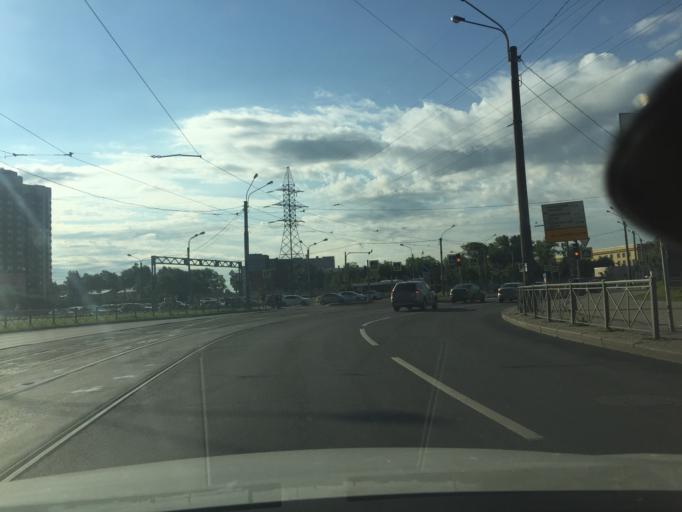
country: RU
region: St.-Petersburg
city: Kupchino
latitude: 59.8320
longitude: 30.3505
